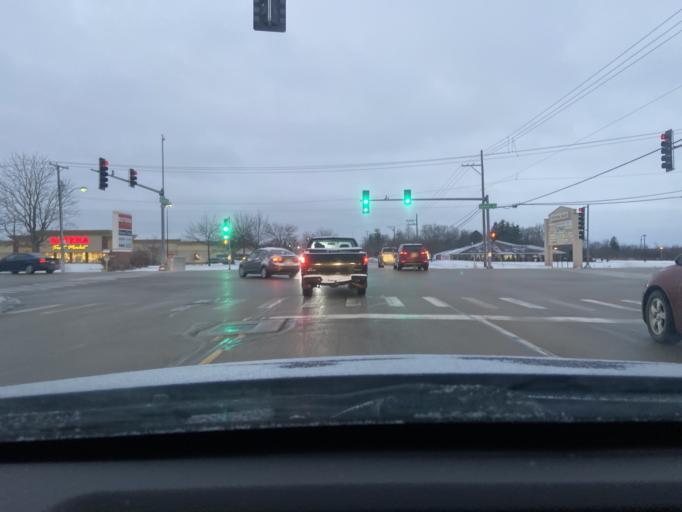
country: US
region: Illinois
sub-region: Lake County
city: Grayslake
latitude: 42.3448
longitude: -88.0241
